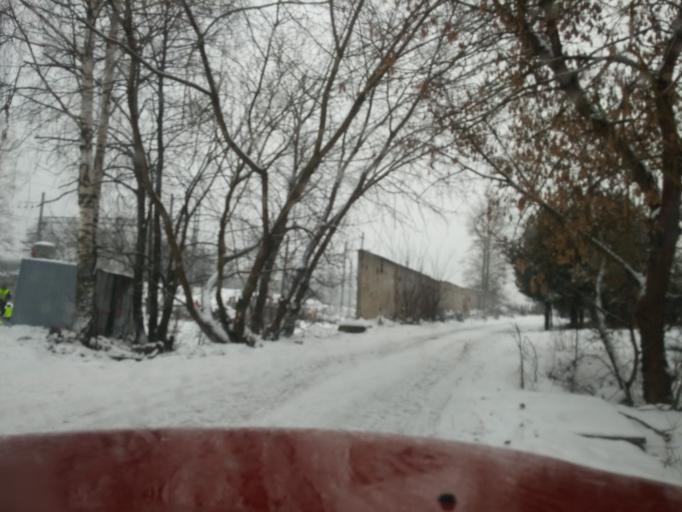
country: RU
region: Tverskaya
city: Novozavidovskiy
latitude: 56.5503
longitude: 36.4395
